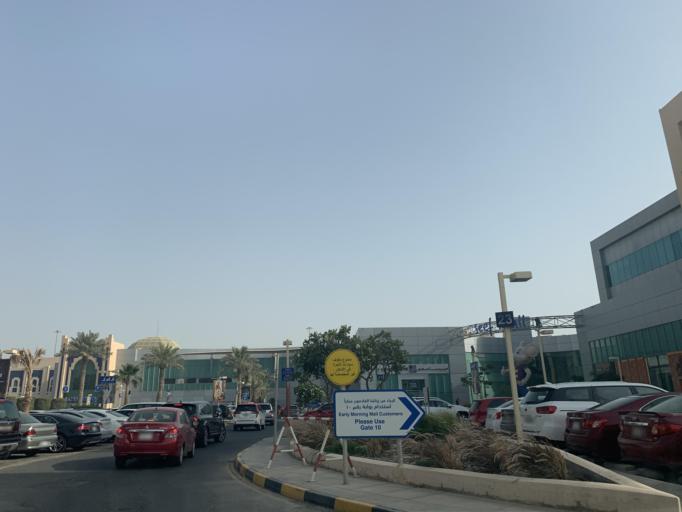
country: BH
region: Manama
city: Jidd Hafs
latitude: 26.2335
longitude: 50.5358
